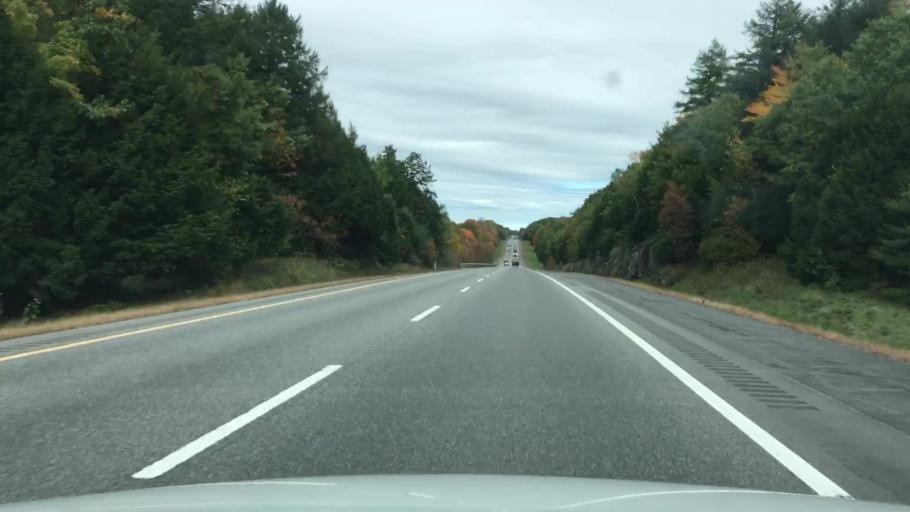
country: US
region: Maine
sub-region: Kennebec County
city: Sidney
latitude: 44.3970
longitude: -69.7543
